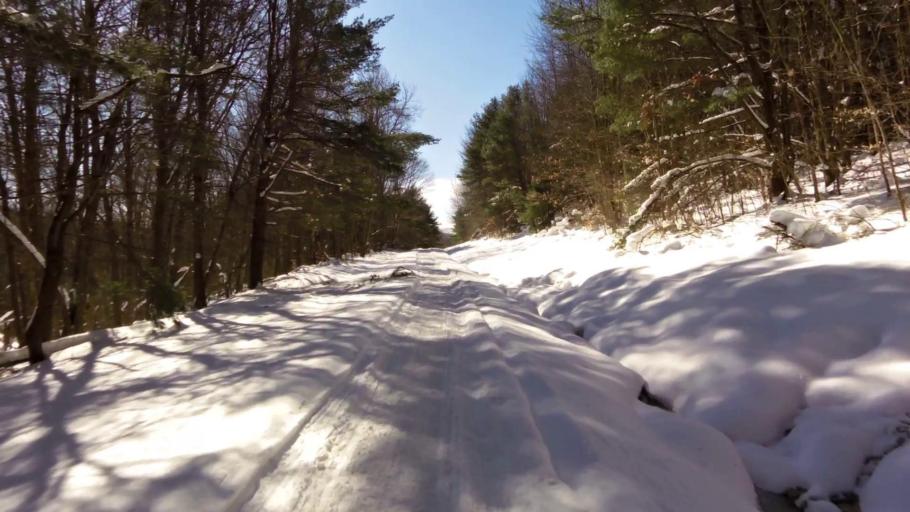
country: US
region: New York
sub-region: Allegany County
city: Cuba
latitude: 42.2911
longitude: -78.2381
